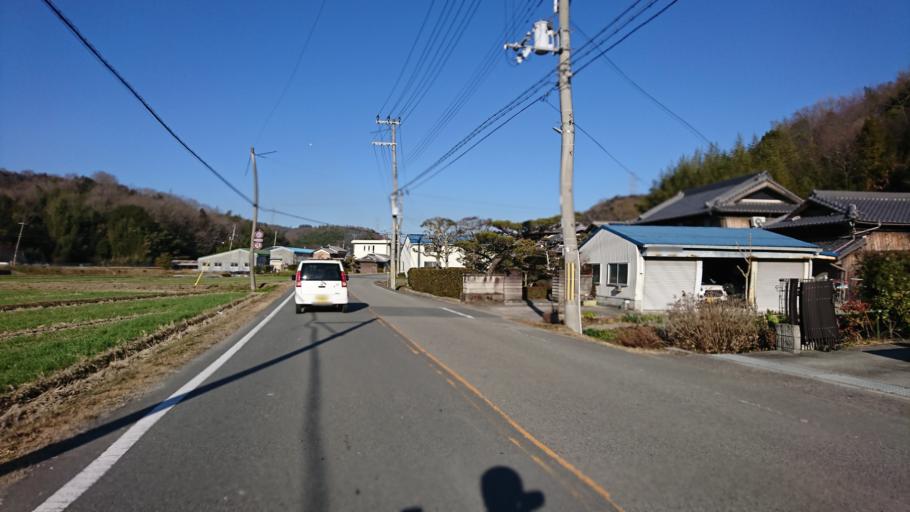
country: JP
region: Hyogo
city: Ono
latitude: 34.8399
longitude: 134.8647
